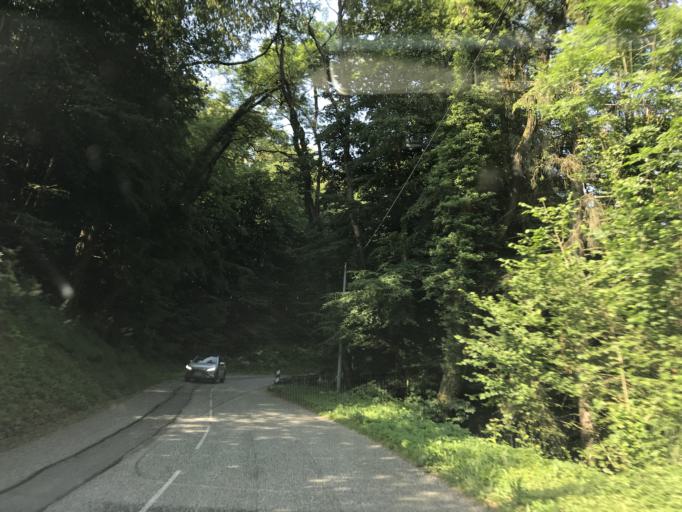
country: FR
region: Rhone-Alpes
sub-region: Departement de la Savoie
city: La Rochette
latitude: 45.4344
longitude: 6.1087
